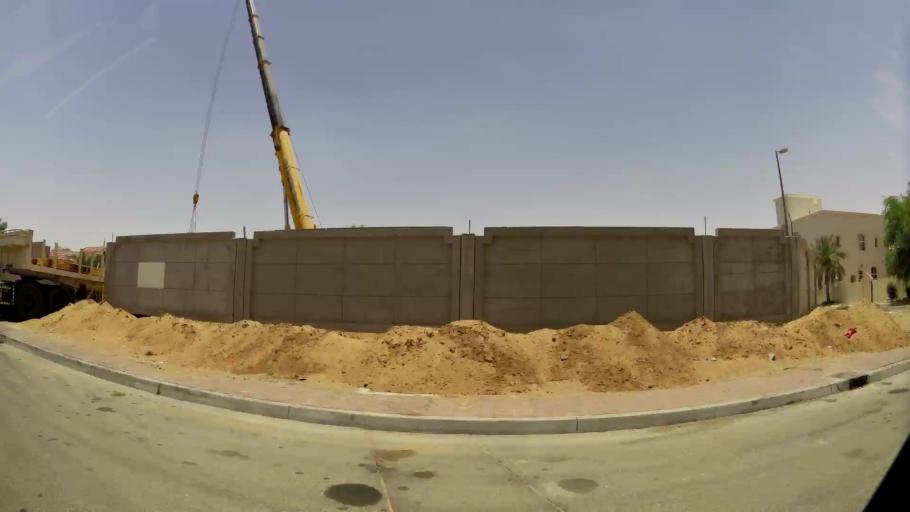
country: OM
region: Al Buraimi
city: Al Buraymi
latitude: 24.2655
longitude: 55.7356
